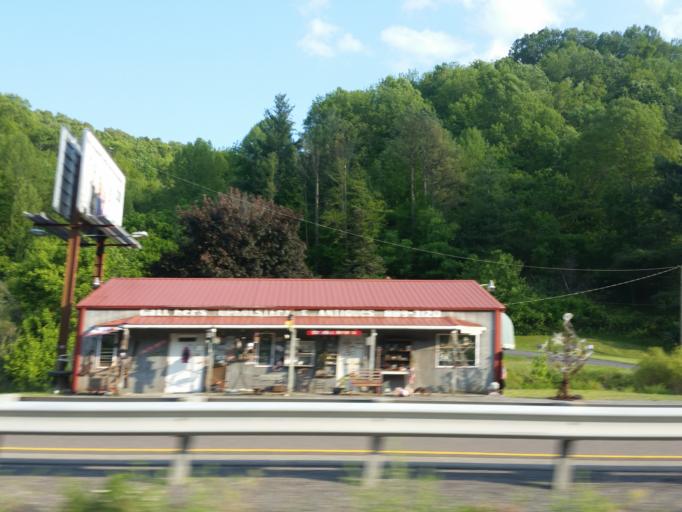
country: US
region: Virginia
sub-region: Russell County
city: Lebanon
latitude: 36.9117
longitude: -82.0204
